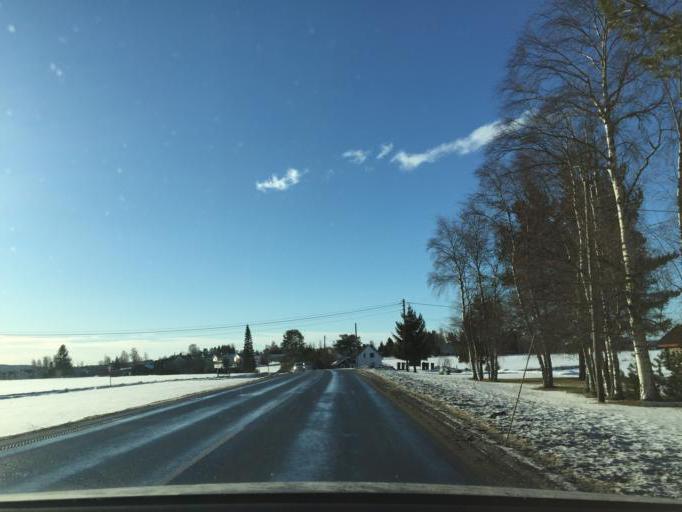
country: NO
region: Akershus
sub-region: Nes
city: Arnes
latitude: 60.1379
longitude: 11.4889
